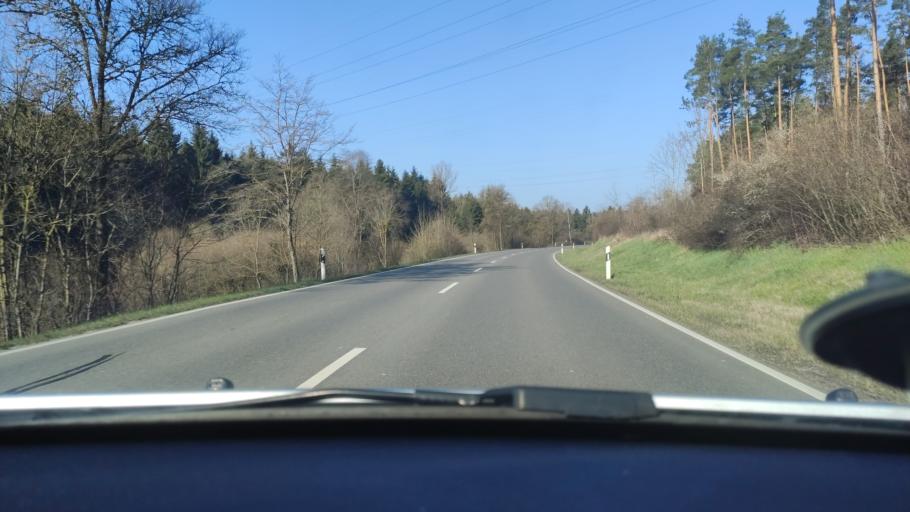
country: DE
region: Baden-Wuerttemberg
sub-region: Tuebingen Region
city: Grosselfingen
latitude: 48.3138
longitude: 8.8788
